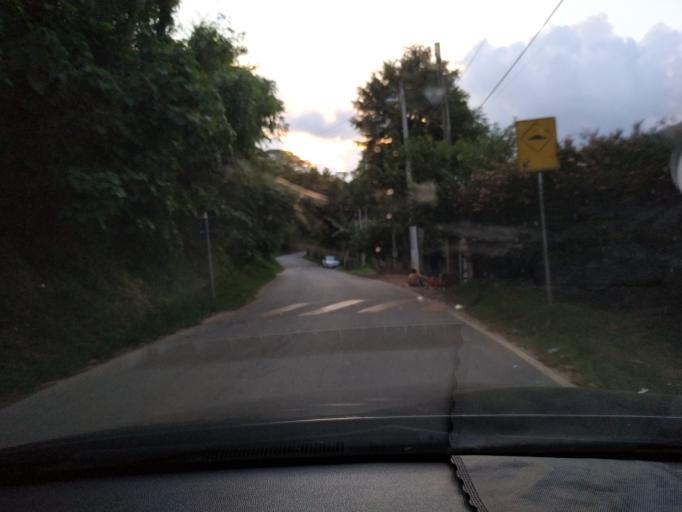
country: BR
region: Sao Paulo
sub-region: Campos Do Jordao
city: Campos do Jordao
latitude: -22.8130
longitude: -45.6572
